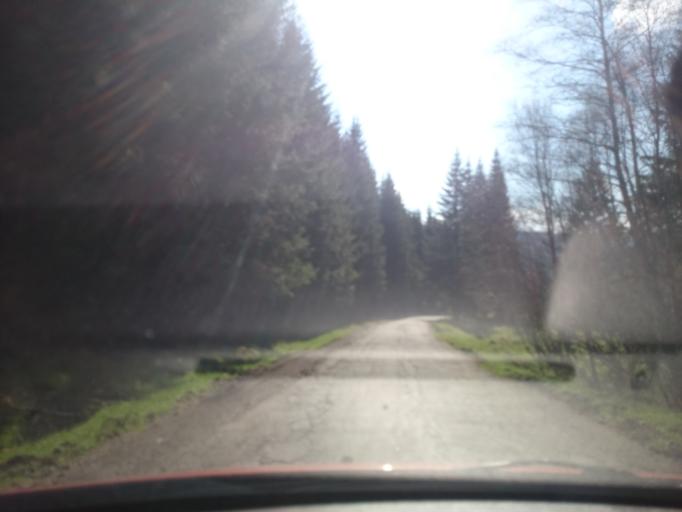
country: PL
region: Lower Silesian Voivodeship
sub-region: Powiat klodzki
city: Polanica-Zdroj
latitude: 50.2978
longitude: 16.4729
